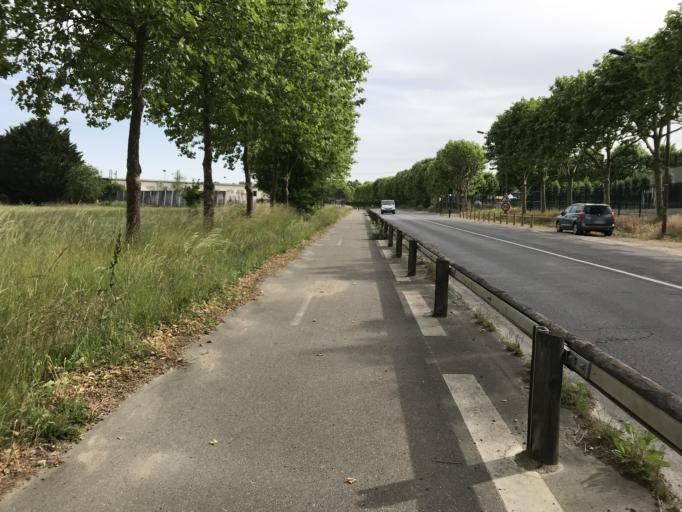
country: FR
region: Ile-de-France
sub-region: Departement de l'Essonne
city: Montlhery
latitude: 48.6390
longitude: 2.2814
